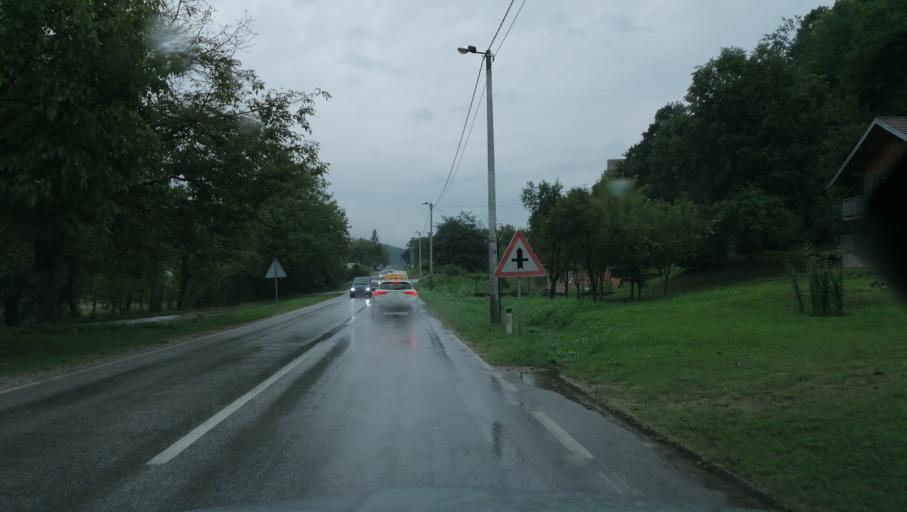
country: BA
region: Federation of Bosnia and Herzegovina
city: Gorazde
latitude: 43.6784
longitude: 19.0325
